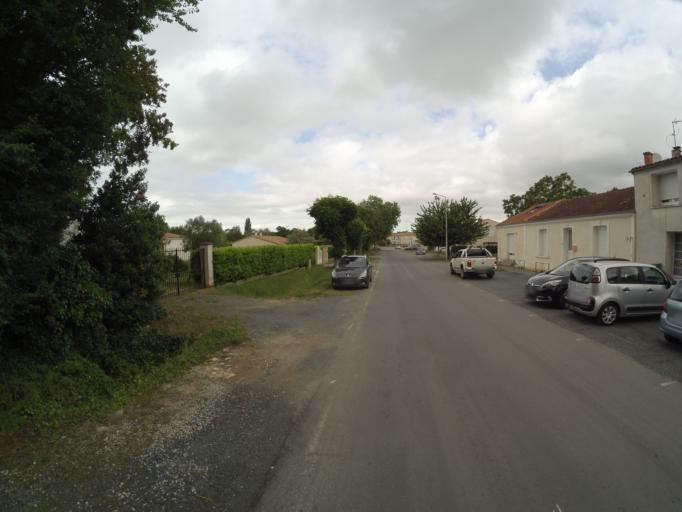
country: FR
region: Poitou-Charentes
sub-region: Departement de la Charente-Maritime
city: Saint-Laurent-de-la-Pree
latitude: 45.9922
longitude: -1.0241
